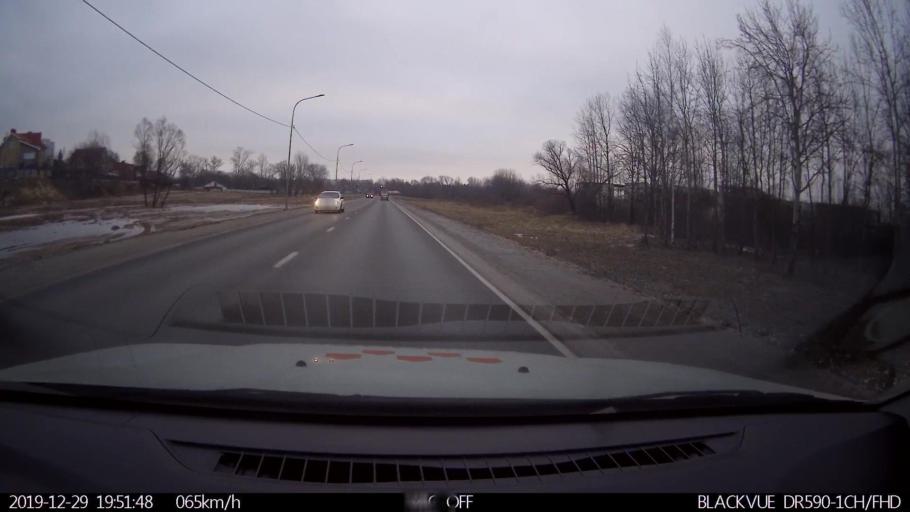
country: RU
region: Nizjnij Novgorod
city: Bor
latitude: 56.3582
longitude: 44.0467
